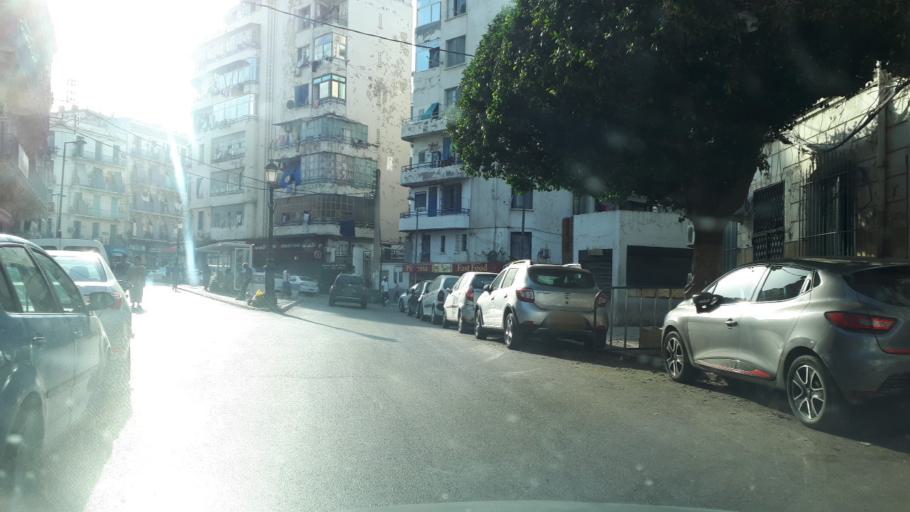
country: DZ
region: Alger
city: Algiers
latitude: 36.7919
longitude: 3.0531
